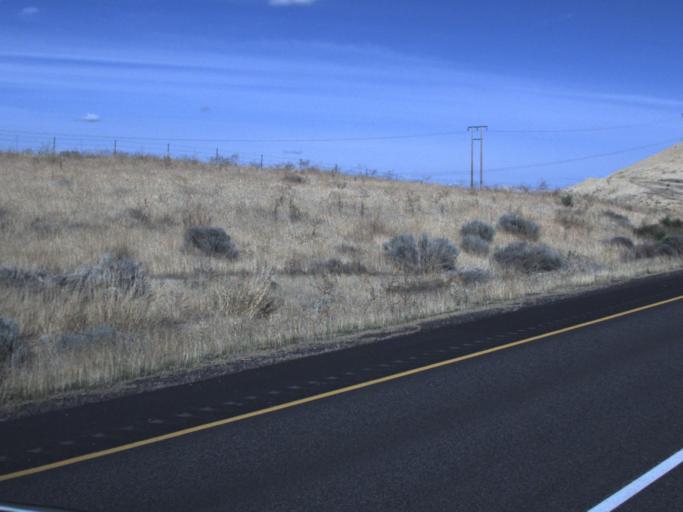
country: US
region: Washington
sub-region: Benton County
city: Prosser
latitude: 46.2200
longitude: -119.6878
